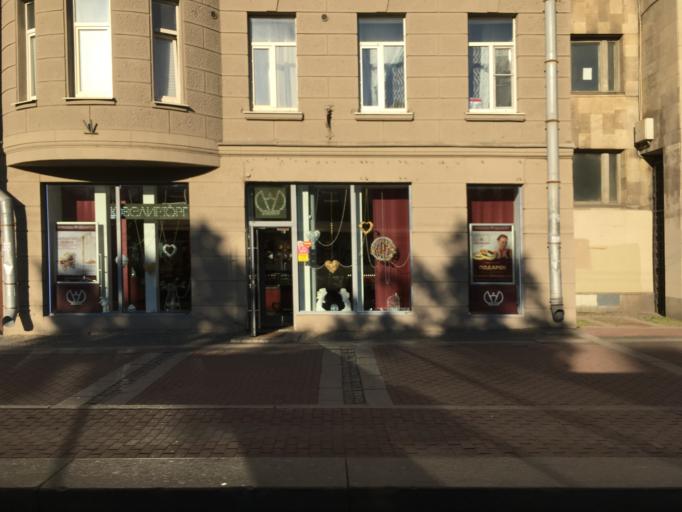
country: RU
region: St.-Petersburg
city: Admiralteisky
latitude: 59.8865
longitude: 30.3202
